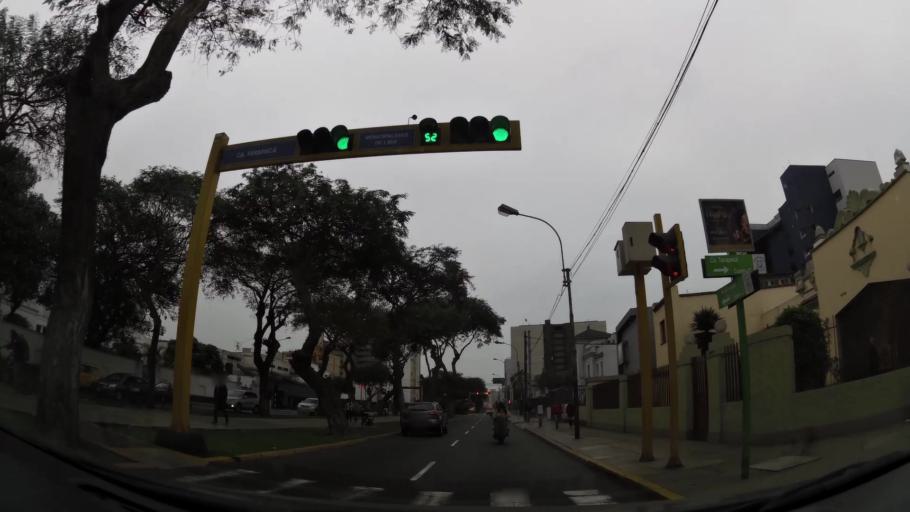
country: PE
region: Lima
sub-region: Lima
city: San Isidro
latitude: -12.1127
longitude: -77.0301
